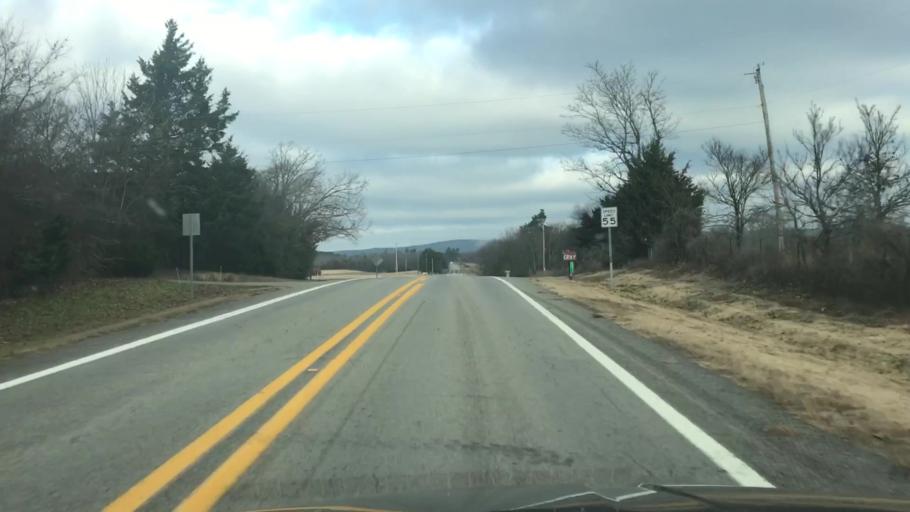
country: US
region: Arkansas
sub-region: Montgomery County
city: Mount Ida
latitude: 34.6353
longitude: -93.7383
